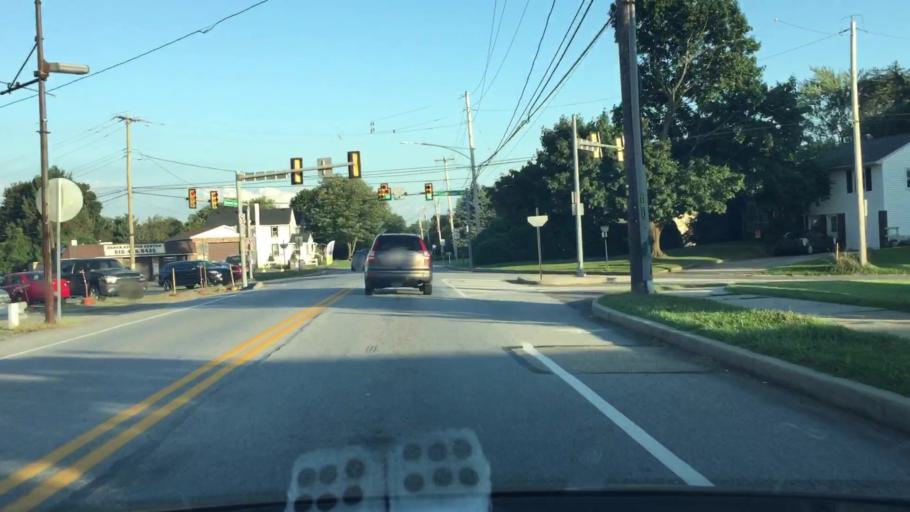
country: US
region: Pennsylvania
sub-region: Delaware County
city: Boothwyn
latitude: 39.8278
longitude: -75.4530
